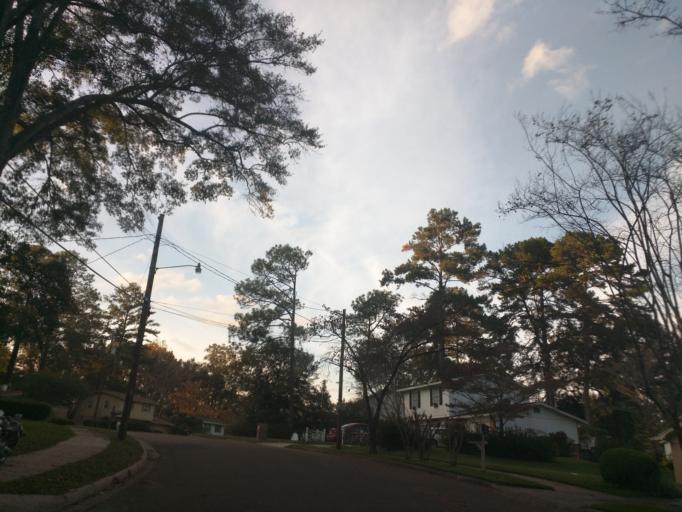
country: US
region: Florida
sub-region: Leon County
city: Tallahassee
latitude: 30.4527
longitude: -84.2510
